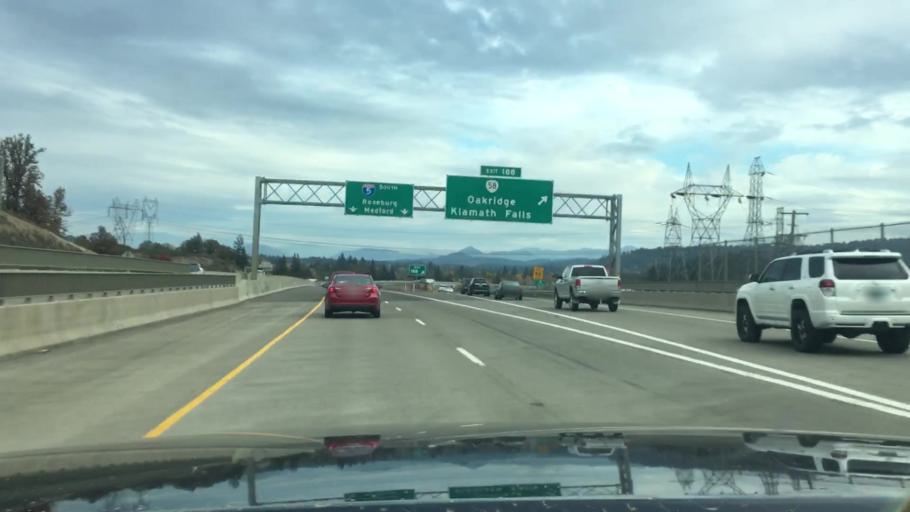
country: US
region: Oregon
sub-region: Lane County
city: Springfield
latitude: 44.0010
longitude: -123.0155
